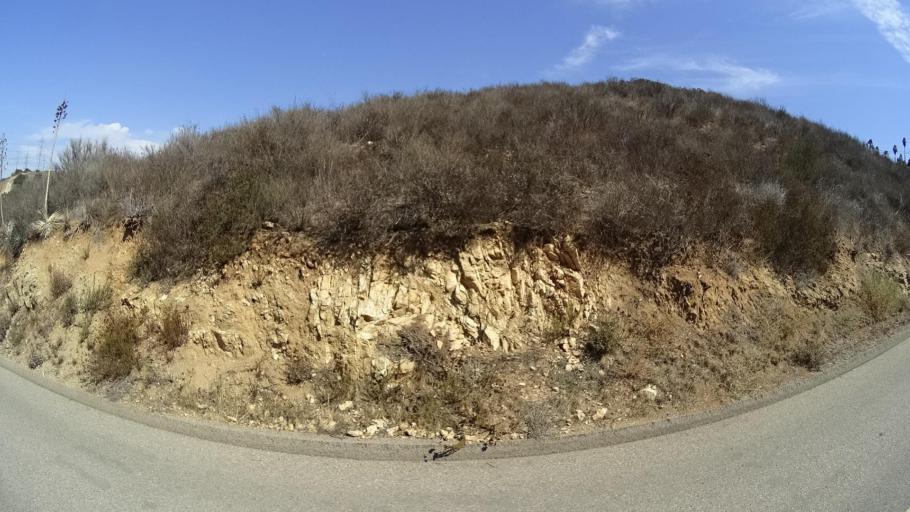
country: US
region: California
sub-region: San Diego County
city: Rancho San Diego
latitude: 32.7203
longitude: -116.9293
